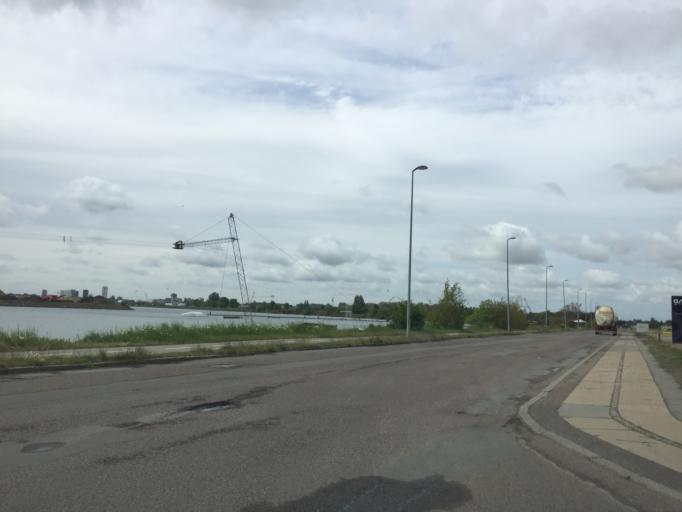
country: DK
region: Capital Region
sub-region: Kobenhavn
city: Christianshavn
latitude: 55.6838
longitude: 12.6245
